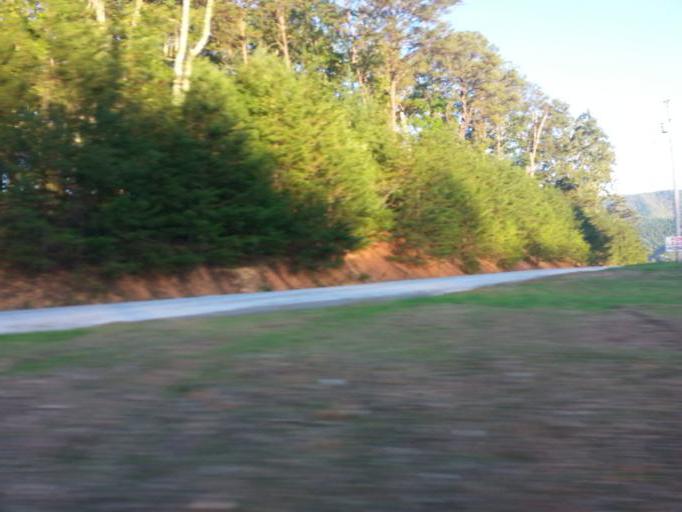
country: US
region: Tennessee
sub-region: Sevier County
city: Pigeon Forge
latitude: 35.7159
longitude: -83.6517
